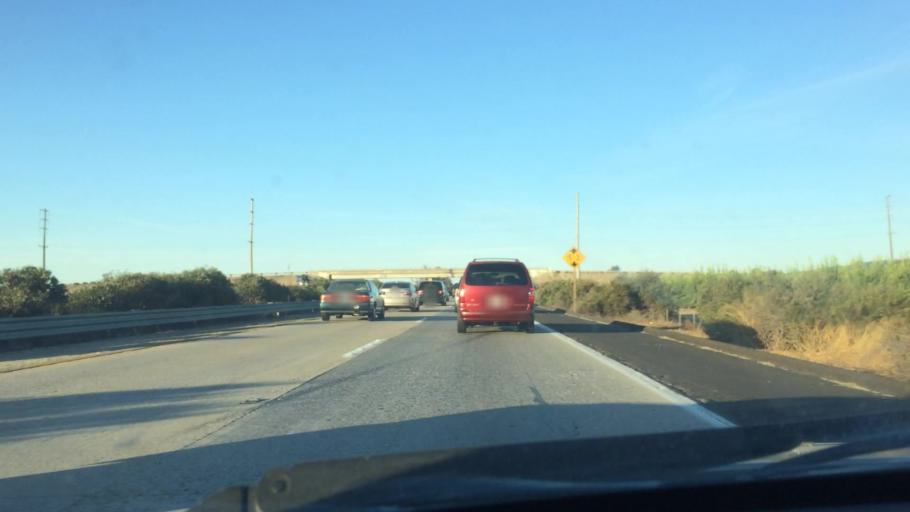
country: US
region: California
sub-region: Ventura County
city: Saticoy
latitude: 34.3070
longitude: -119.1274
